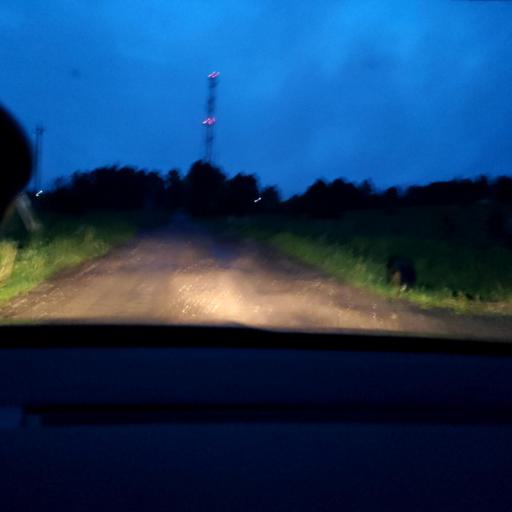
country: RU
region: Moskovskaya
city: Dmitrov
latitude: 56.3247
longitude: 37.5793
